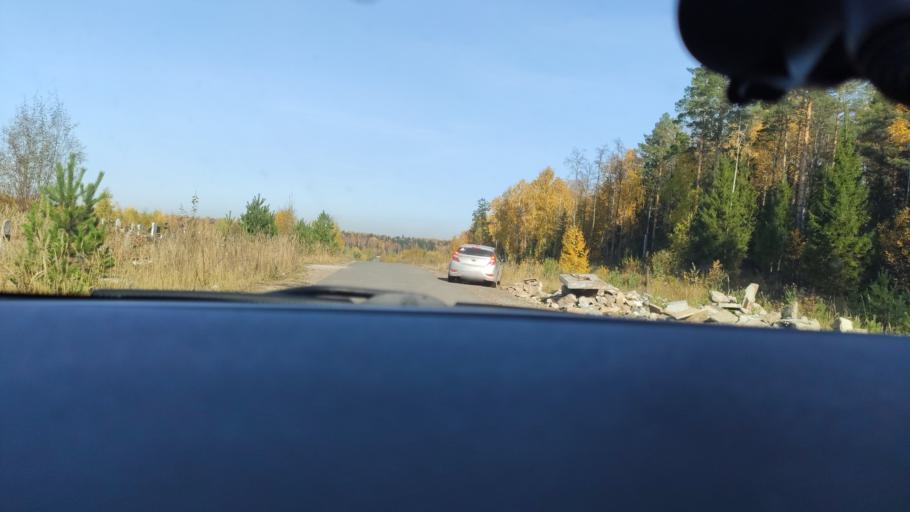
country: RU
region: Perm
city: Kondratovo
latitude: 58.0613
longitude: 56.1608
